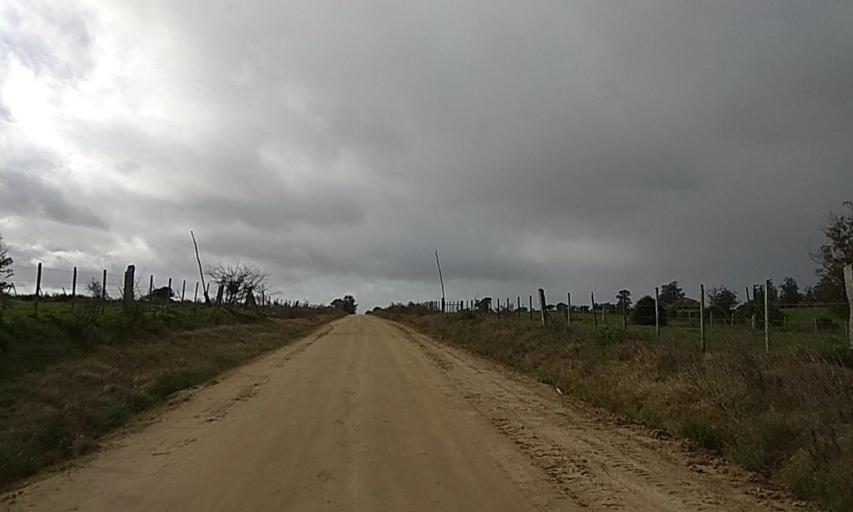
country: UY
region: Florida
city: Florida
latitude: -34.0603
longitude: -56.2094
